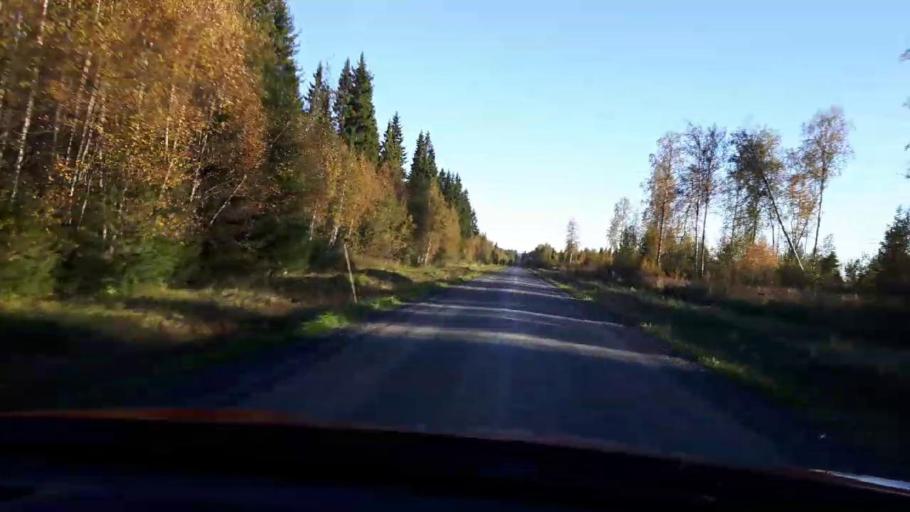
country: SE
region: Jaemtland
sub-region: OEstersunds Kommun
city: Lit
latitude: 63.6536
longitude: 14.7154
